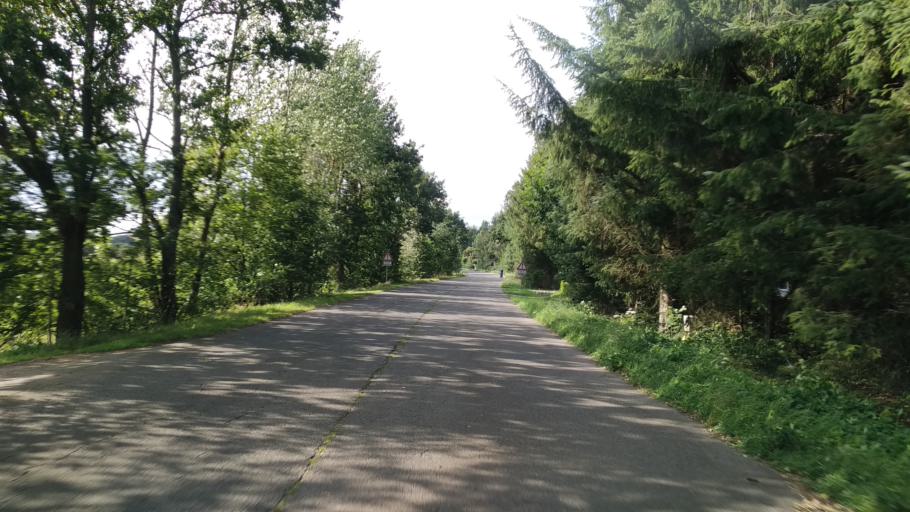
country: DE
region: Schleswig-Holstein
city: Neuberend
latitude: 54.5509
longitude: 9.5391
